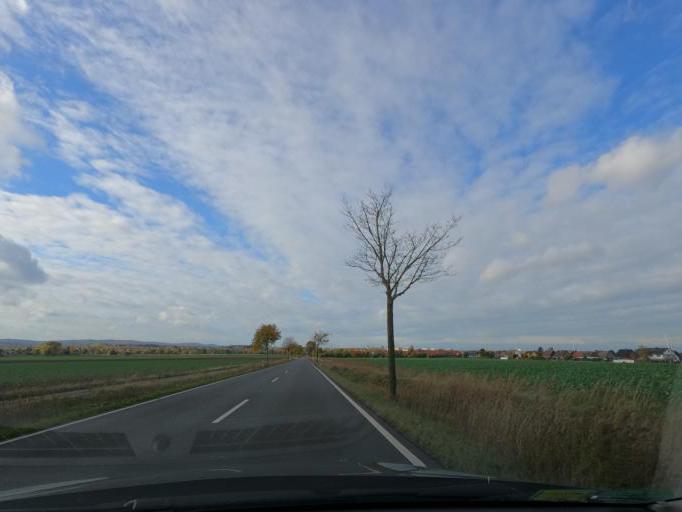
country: DE
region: Lower Saxony
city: Cramme
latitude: 52.1387
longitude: 10.4657
